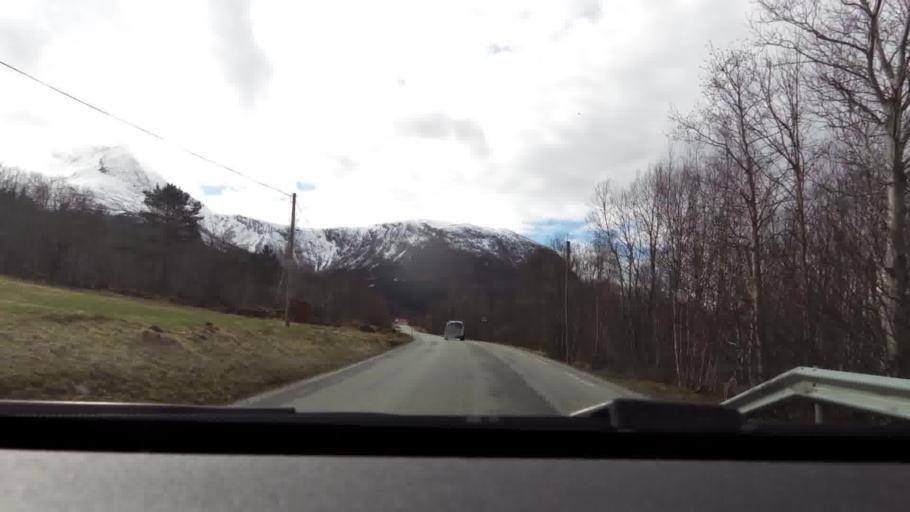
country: NO
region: More og Romsdal
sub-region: Gjemnes
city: Batnfjordsora
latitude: 62.9386
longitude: 7.6053
